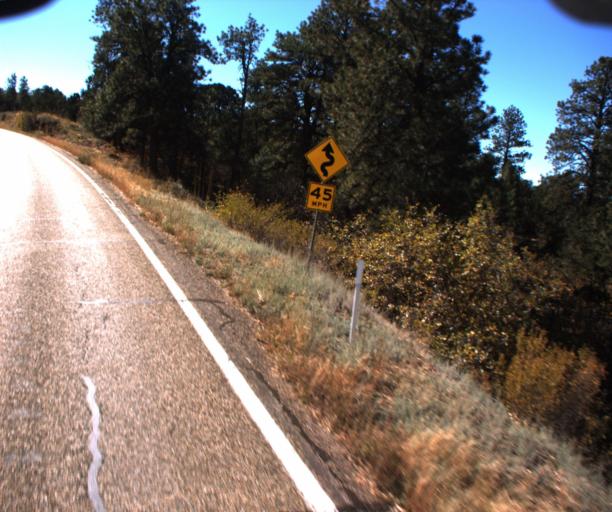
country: US
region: Arizona
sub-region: Coconino County
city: Fredonia
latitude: 36.7859
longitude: -112.2576
